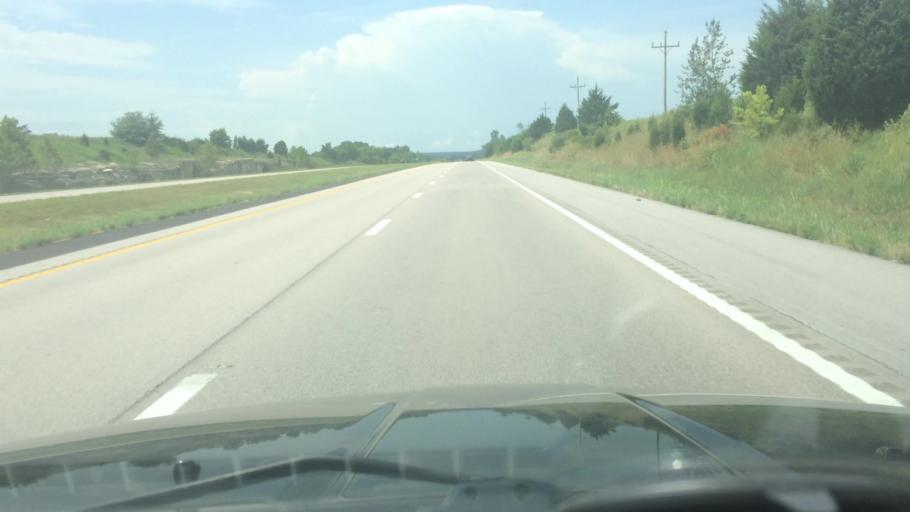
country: US
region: Missouri
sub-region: Polk County
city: Humansville
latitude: 37.8013
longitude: -93.5954
